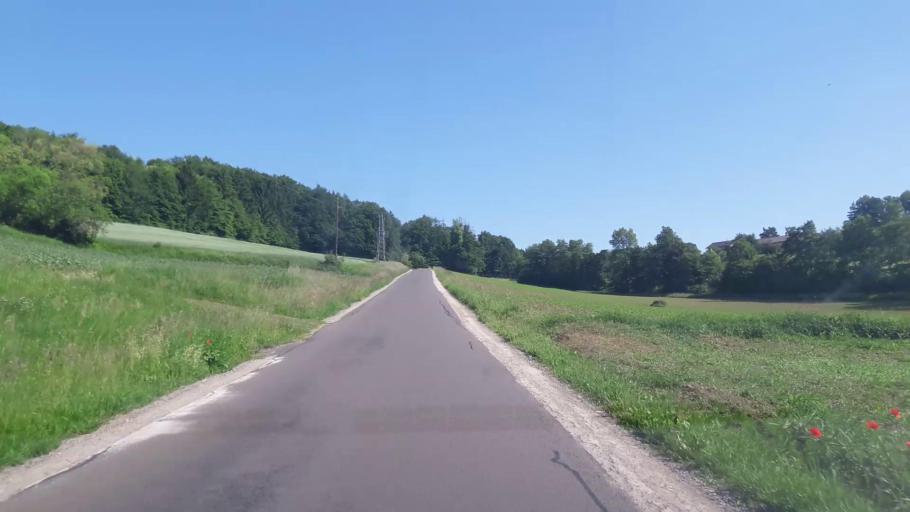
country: AT
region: Styria
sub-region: Politischer Bezirk Hartberg-Fuerstenfeld
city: UEbersbach
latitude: 46.9982
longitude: 16.0445
